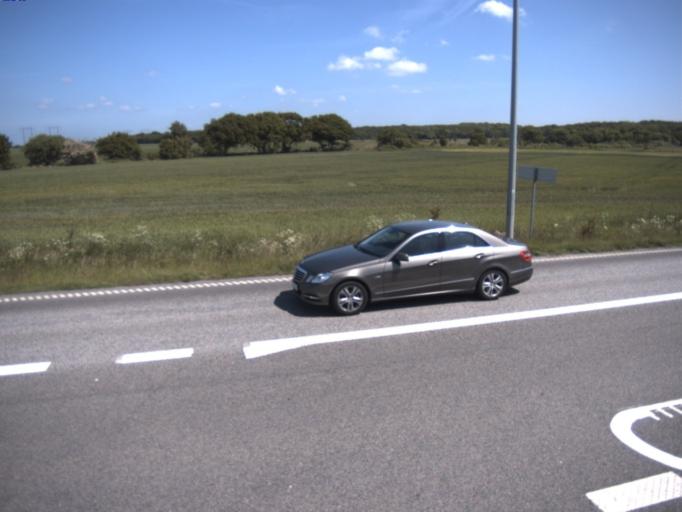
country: DK
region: Capital Region
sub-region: Helsingor Kommune
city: Hellebaek
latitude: 56.1286
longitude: 12.5973
